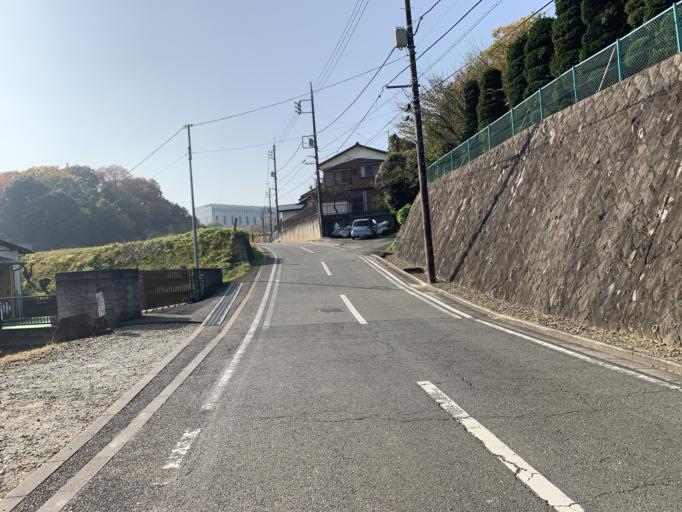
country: JP
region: Tokyo
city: Kokubunji
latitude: 35.6273
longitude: 139.4757
